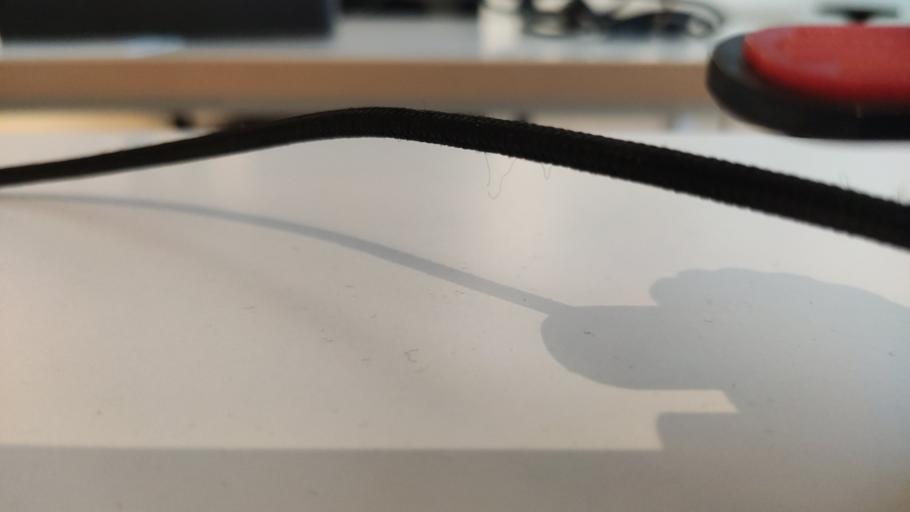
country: RU
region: Moskovskaya
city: Novopetrovskoye
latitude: 55.9312
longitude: 36.4339
